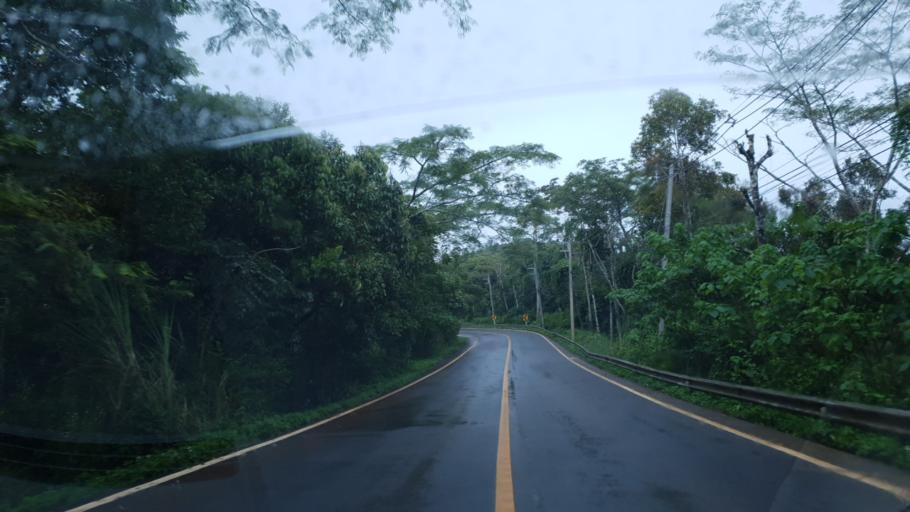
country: TH
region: Mae Hong Son
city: Ban Huai I Huak
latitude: 18.1373
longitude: 98.0769
